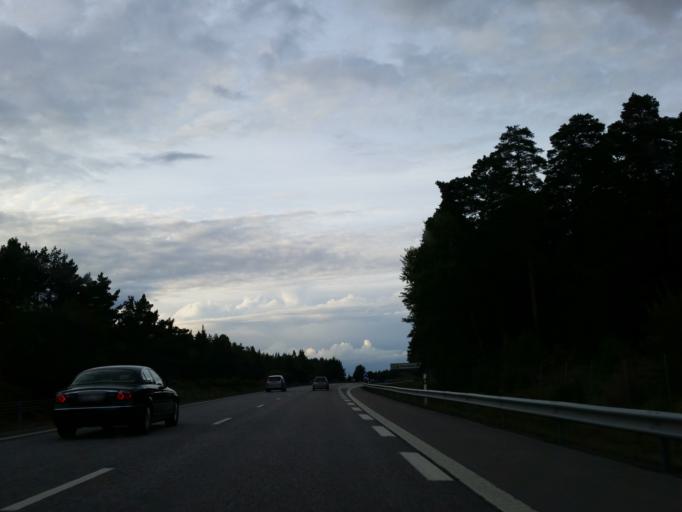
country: SE
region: Uppsala
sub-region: Uppsala Kommun
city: Alsike
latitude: 59.7895
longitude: 17.7758
